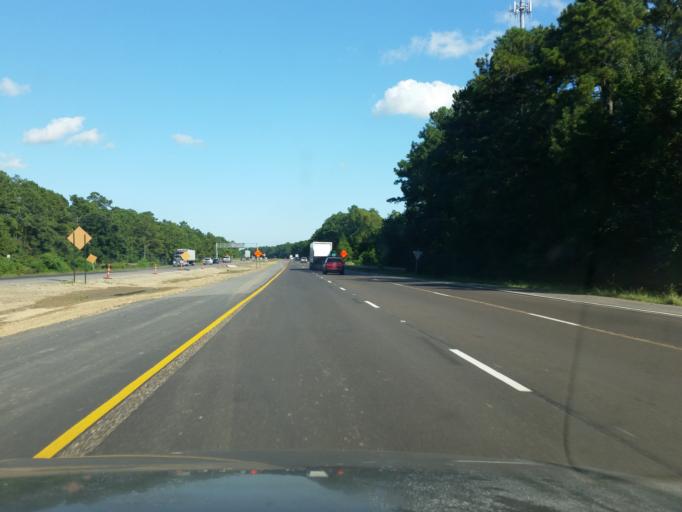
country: US
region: Louisiana
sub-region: Saint Tammany Parish
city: Slidell
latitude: 30.3012
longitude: -89.7236
